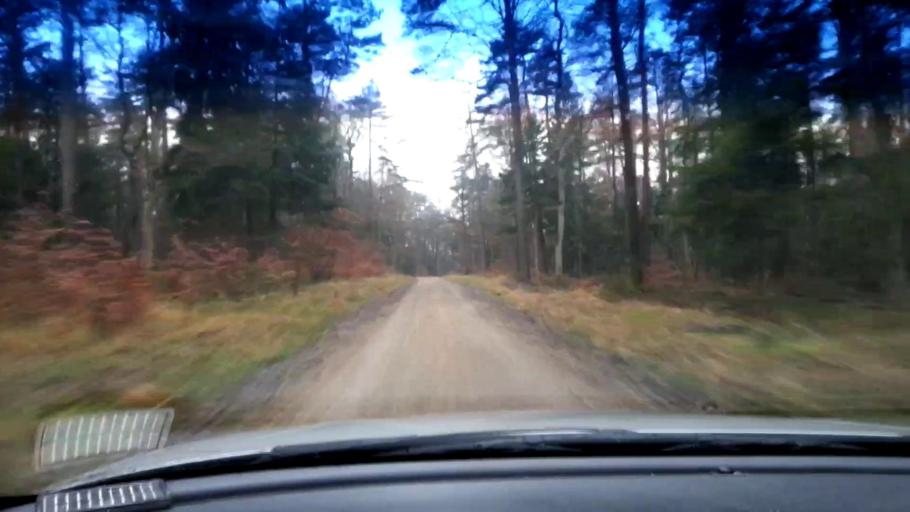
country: DE
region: Bavaria
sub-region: Upper Franconia
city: Gundelsheim
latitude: 49.9532
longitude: 10.9168
